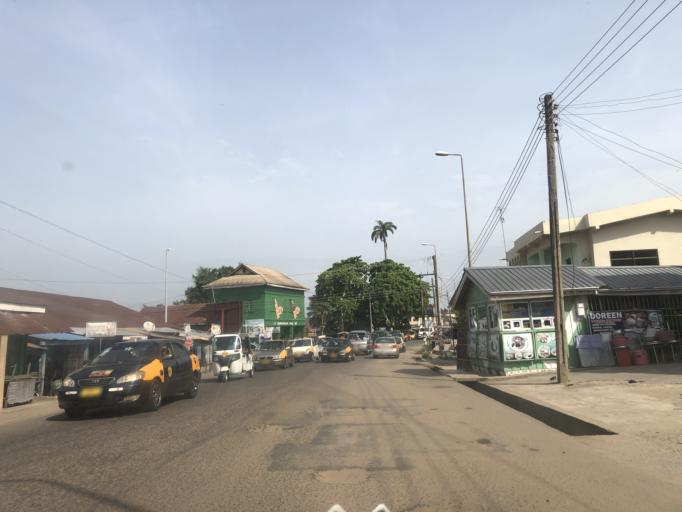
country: GH
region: Eastern
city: Koforidua
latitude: 6.0951
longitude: -0.2608
